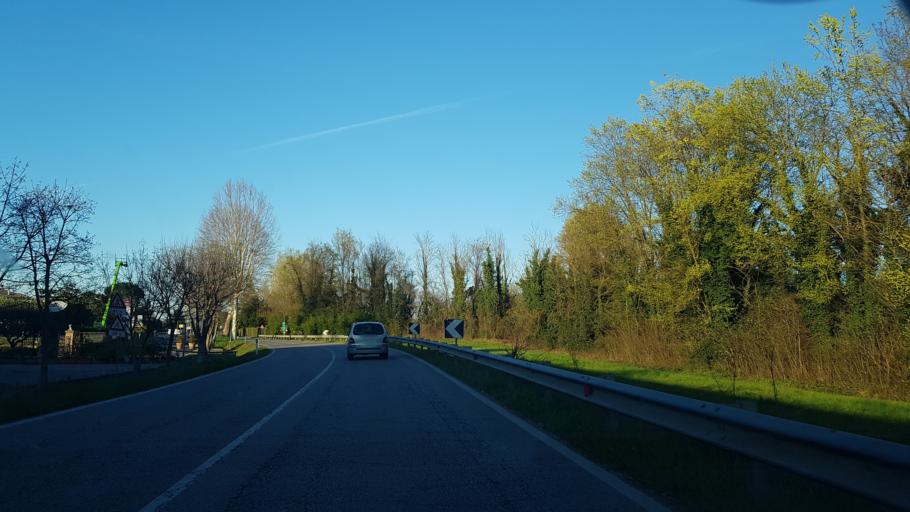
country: IT
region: Veneto
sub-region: Provincia di Vicenza
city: Ponte di Nanto
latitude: 45.4141
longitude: 11.5861
